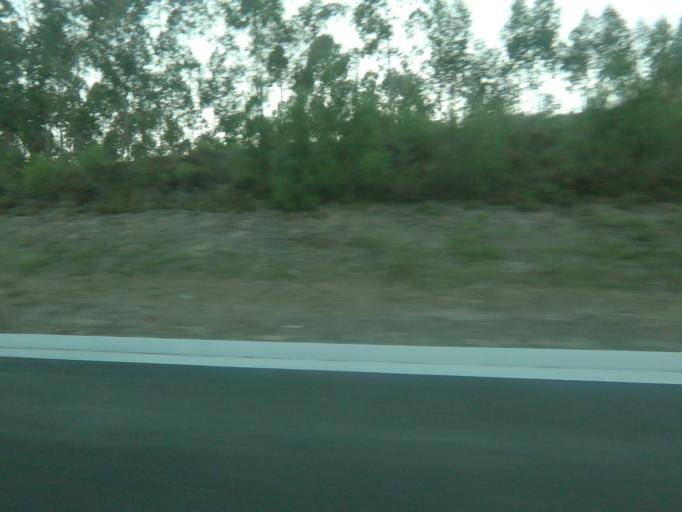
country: PT
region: Leiria
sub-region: Pombal
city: Pombal
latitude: 39.8742
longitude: -8.7022
